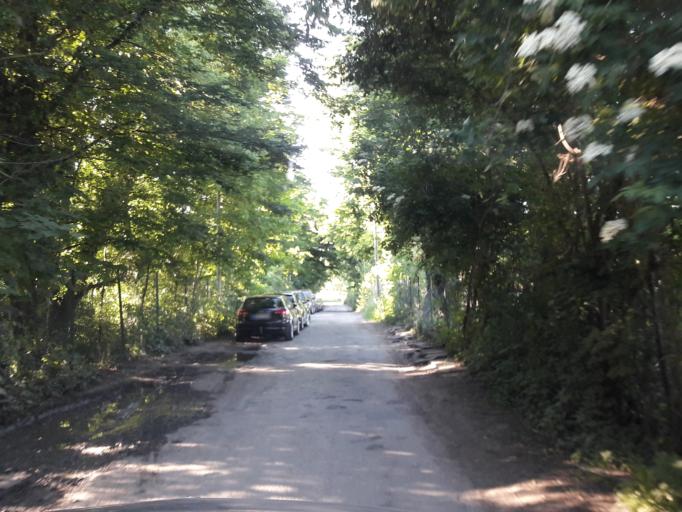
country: DE
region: Rheinland-Pfalz
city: Altrip
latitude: 49.4456
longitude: 8.4706
